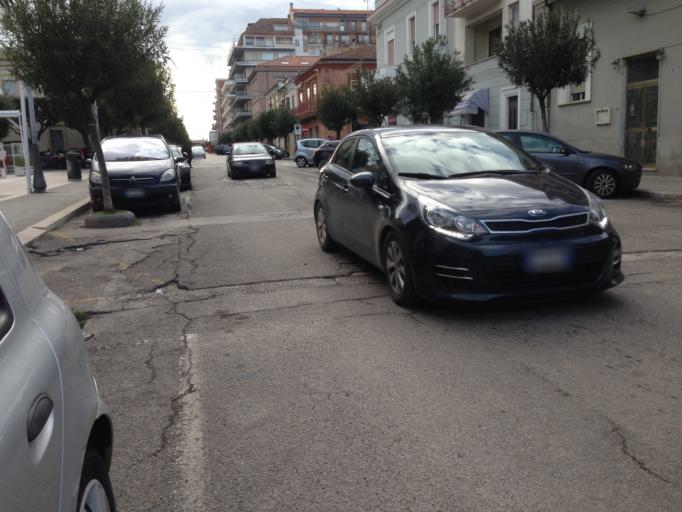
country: IT
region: Molise
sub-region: Provincia di Campobasso
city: Termoli
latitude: 42.0010
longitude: 14.9966
